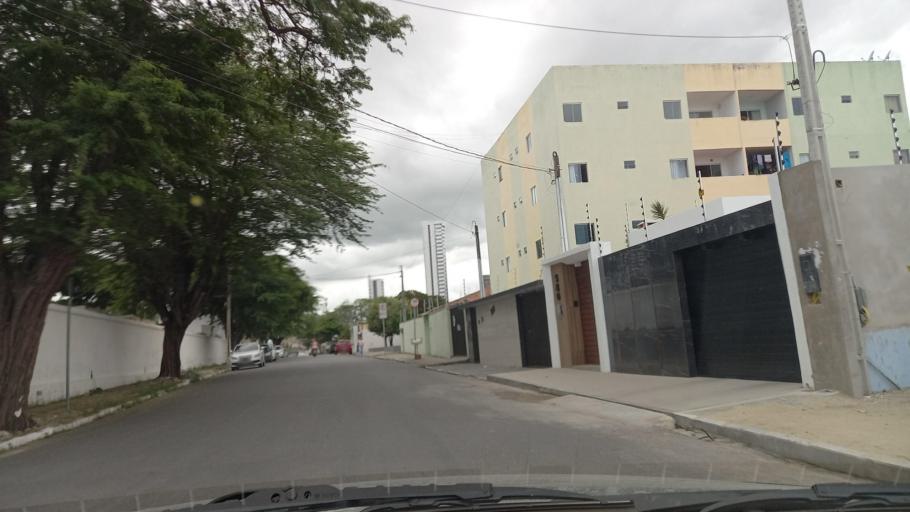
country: BR
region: Pernambuco
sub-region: Caruaru
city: Caruaru
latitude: -8.2753
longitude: -35.9677
